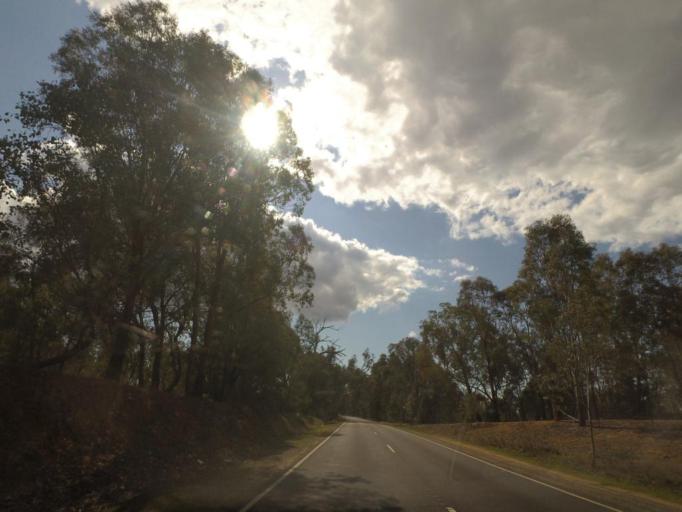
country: AU
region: New South Wales
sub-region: Corowa Shire
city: Howlong
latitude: -36.1735
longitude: 146.6078
